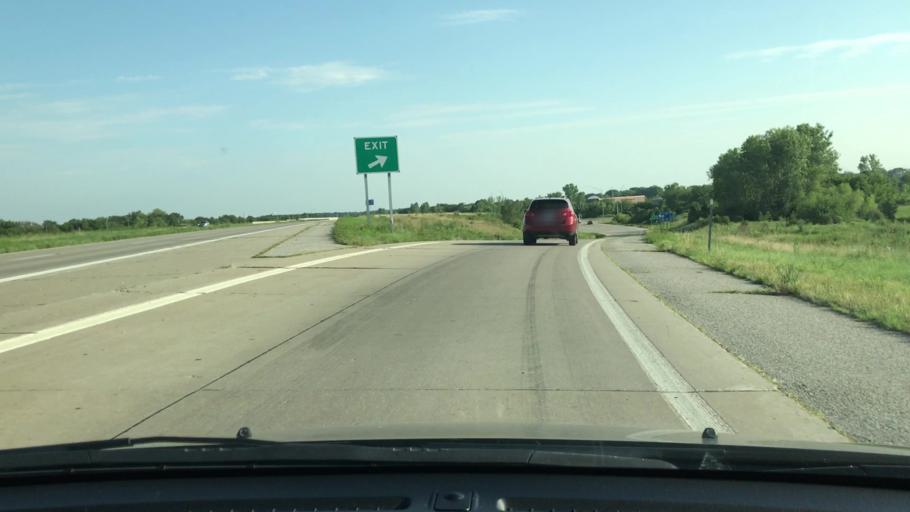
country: US
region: Missouri
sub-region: Cass County
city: Lake Winnebago
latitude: 38.8557
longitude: -94.3759
